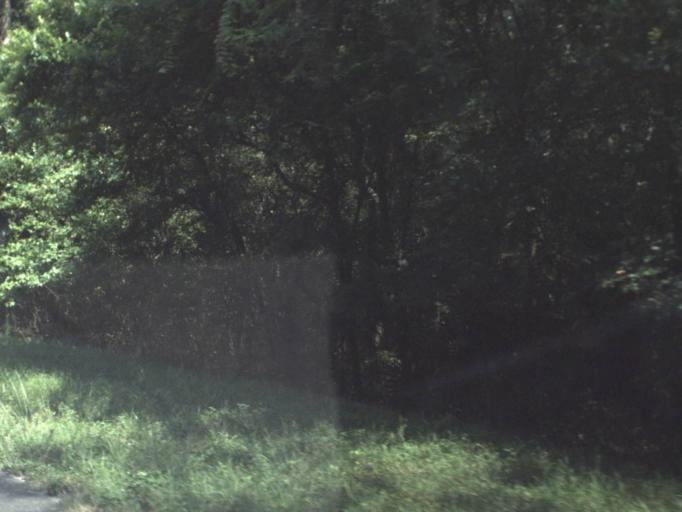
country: US
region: Florida
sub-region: Duval County
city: Jacksonville
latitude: 30.3228
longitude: -81.7726
